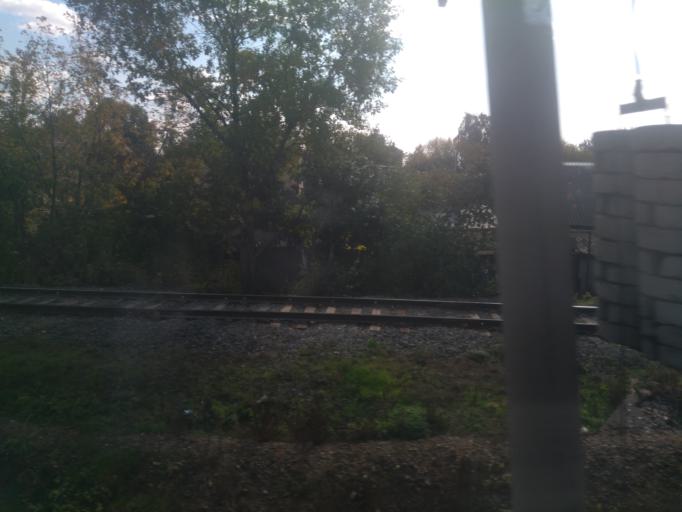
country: RU
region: Tatarstan
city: Verkhniy Uslon
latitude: 55.8013
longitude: 49.0239
